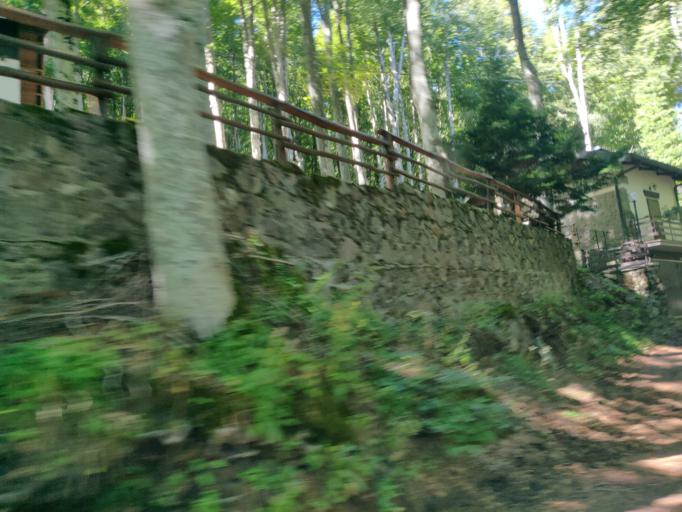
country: IT
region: Tuscany
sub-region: Provincia di Siena
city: Abbadia San Salvatore
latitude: 42.8966
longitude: 11.6282
